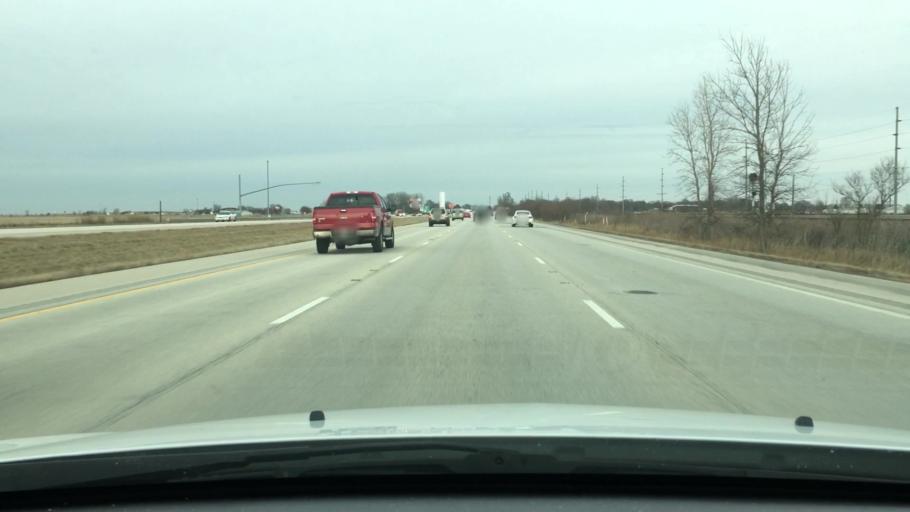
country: US
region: Illinois
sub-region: Sangamon County
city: Williamsville
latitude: 39.9403
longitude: -89.5620
